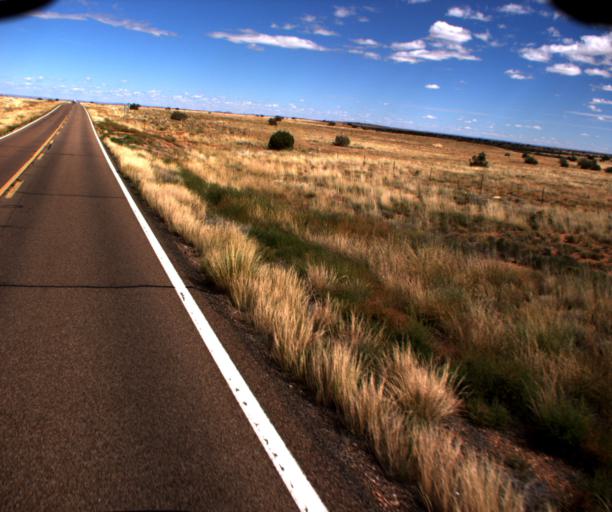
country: US
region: Arizona
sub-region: Navajo County
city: Holbrook
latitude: 34.7366
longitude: -110.2756
